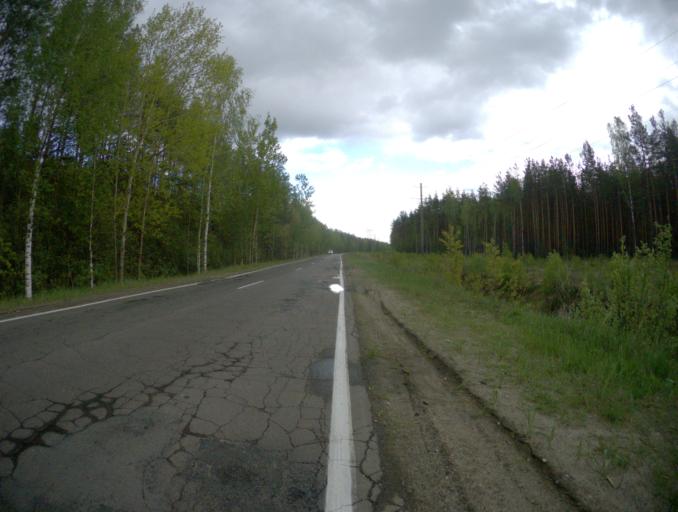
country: RU
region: Vladimir
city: Mezinovskiy
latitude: 55.5946
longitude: 40.3993
